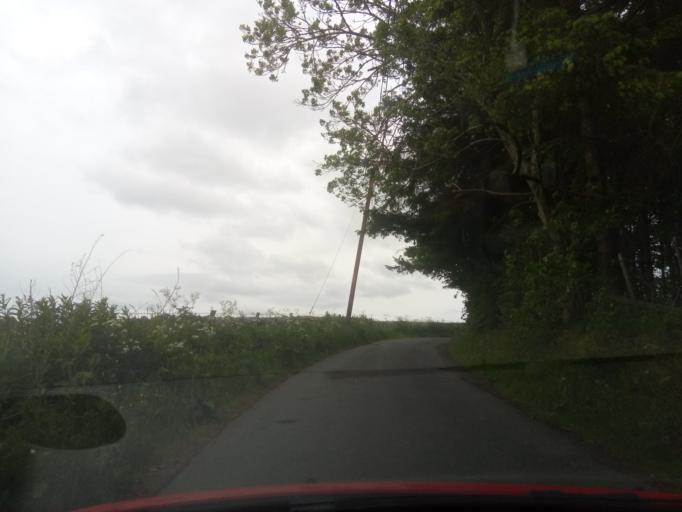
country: GB
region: Scotland
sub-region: The Scottish Borders
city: Selkirk
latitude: 55.5535
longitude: -2.8242
